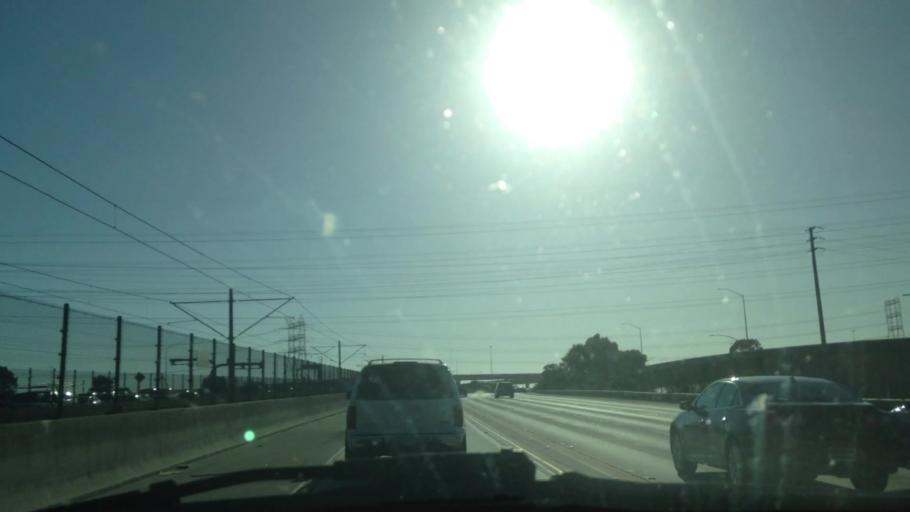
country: US
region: California
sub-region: Los Angeles County
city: Paramount
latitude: 33.9110
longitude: -118.1718
